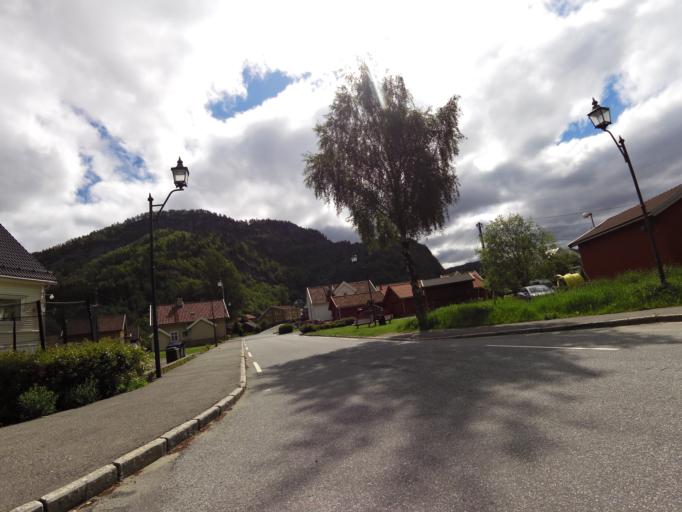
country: NO
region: Vest-Agder
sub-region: Kvinesdal
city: Liknes
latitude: 58.2712
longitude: 6.8132
